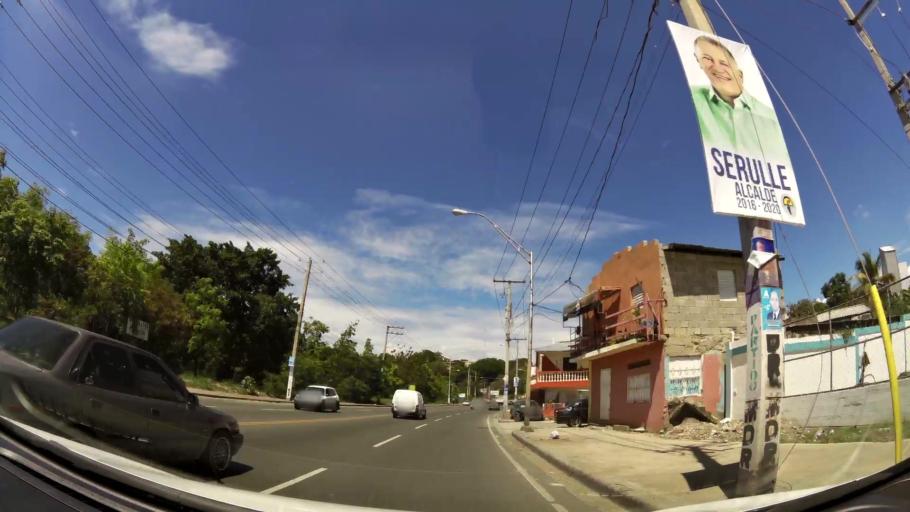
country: DO
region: Santiago
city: Santiago de los Caballeros
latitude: 19.4436
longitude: -70.7034
